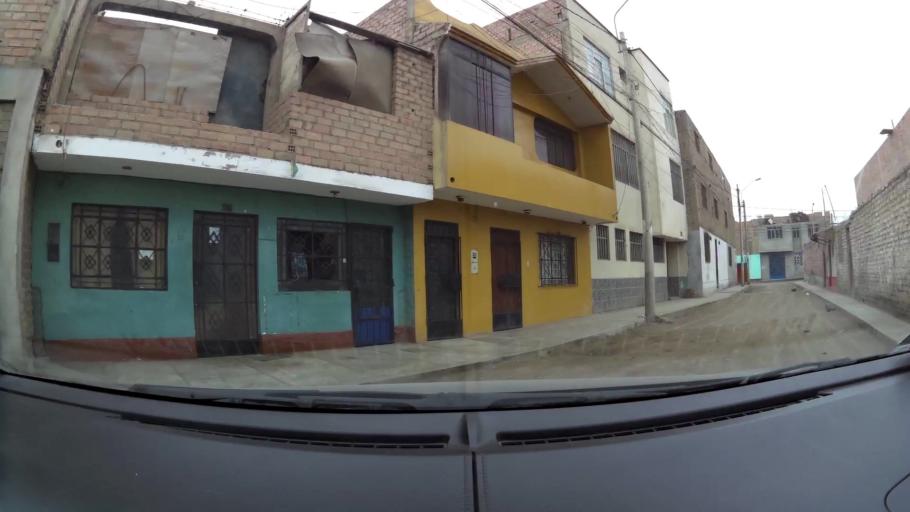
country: PE
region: Lima
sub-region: Barranca
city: Barranca
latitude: -10.7491
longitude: -77.7554
